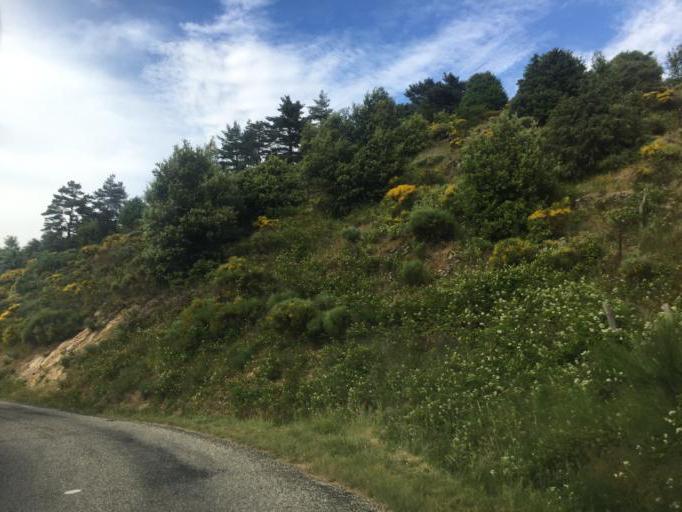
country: FR
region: Rhone-Alpes
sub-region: Departement de l'Ardeche
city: Flaviac
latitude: 44.7937
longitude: 4.6732
